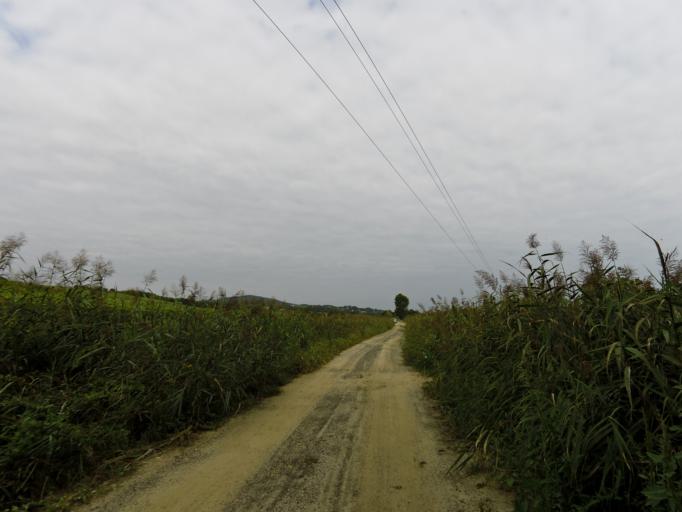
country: HU
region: Veszprem
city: Tapolca
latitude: 46.8399
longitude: 17.3669
